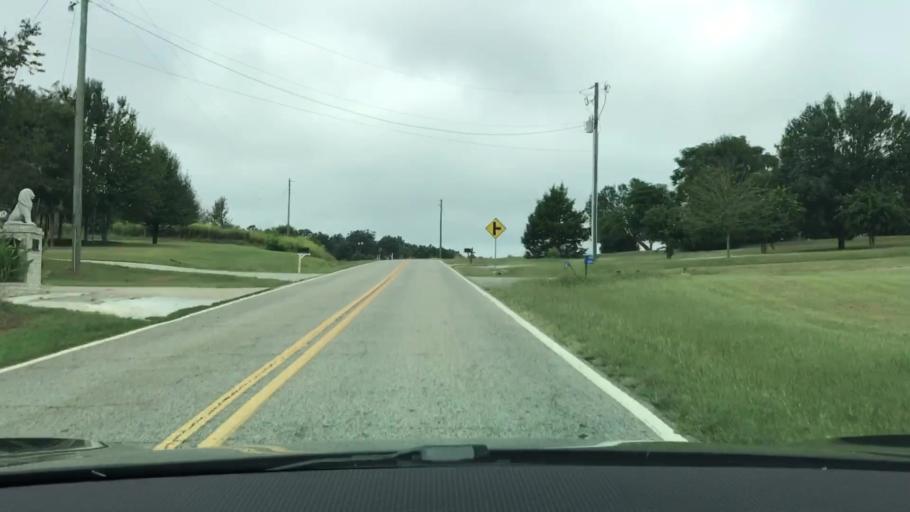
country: US
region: Georgia
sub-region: Barrow County
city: Auburn
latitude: 34.0389
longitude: -83.8025
